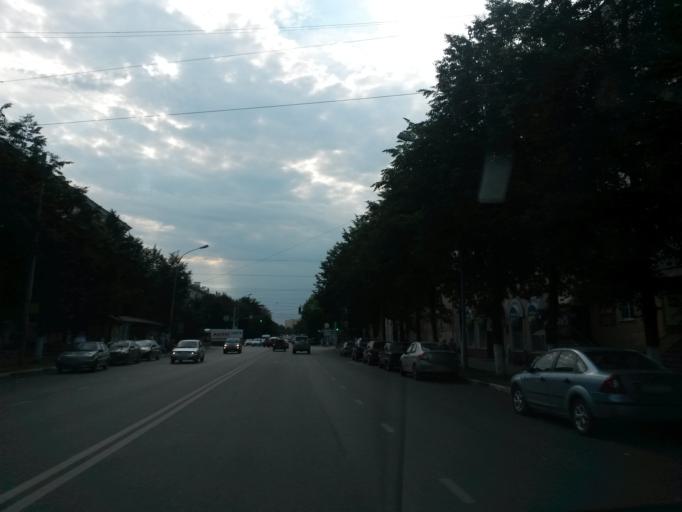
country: RU
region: Jaroslavl
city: Yaroslavl
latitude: 57.6265
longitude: 39.8597
